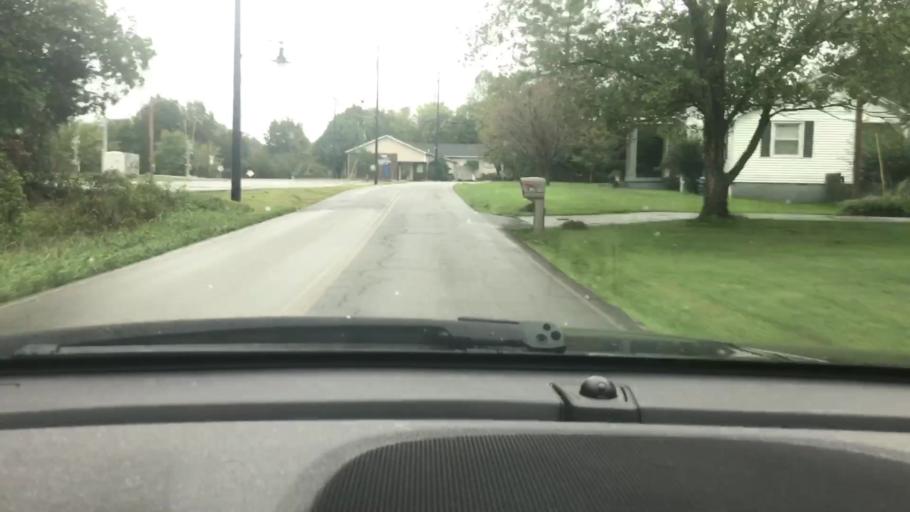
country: US
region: Tennessee
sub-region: Cheatham County
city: Kingston Springs
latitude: 36.1016
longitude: -87.1161
